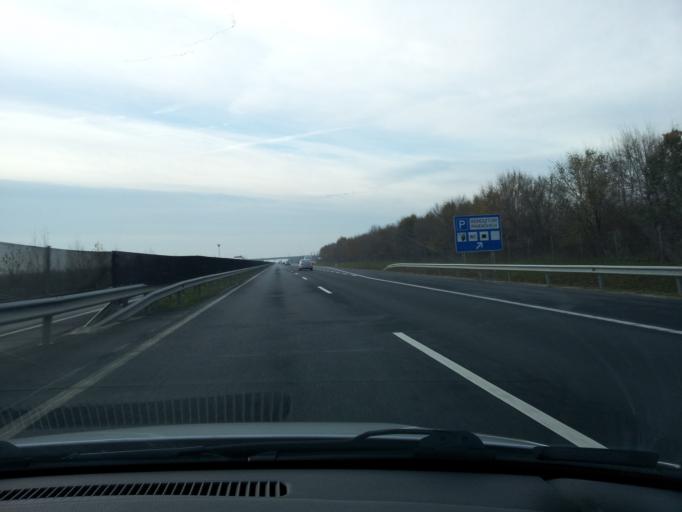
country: HU
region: Fejer
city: Rackeresztur
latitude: 47.2909
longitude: 18.8641
